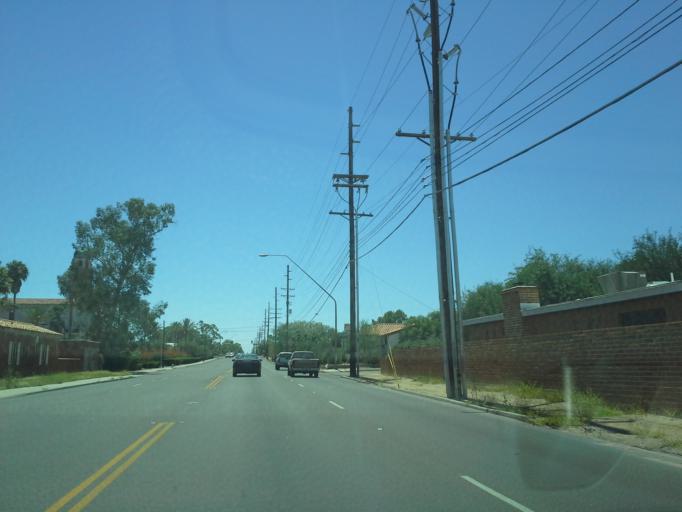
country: US
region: Arizona
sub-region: Pima County
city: Tucson
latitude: 32.2345
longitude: -110.9268
